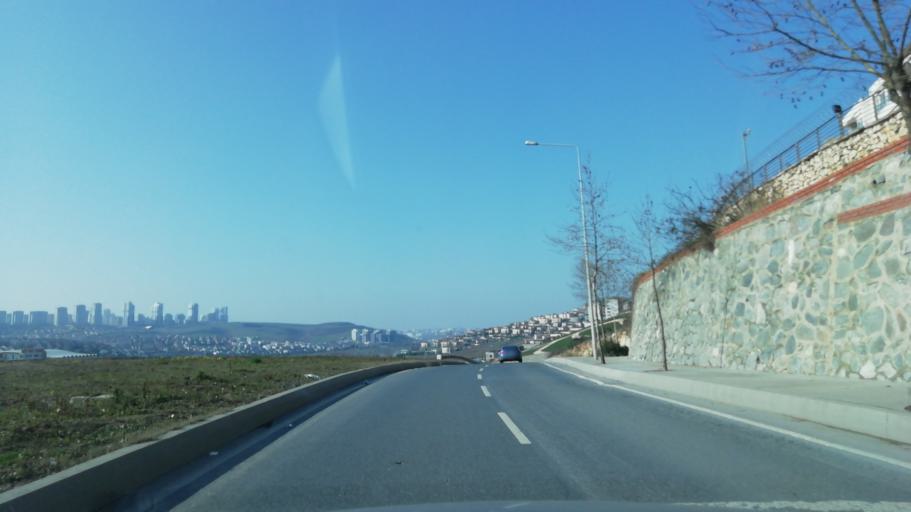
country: TR
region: Istanbul
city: Esenyurt
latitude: 41.0770
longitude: 28.6890
